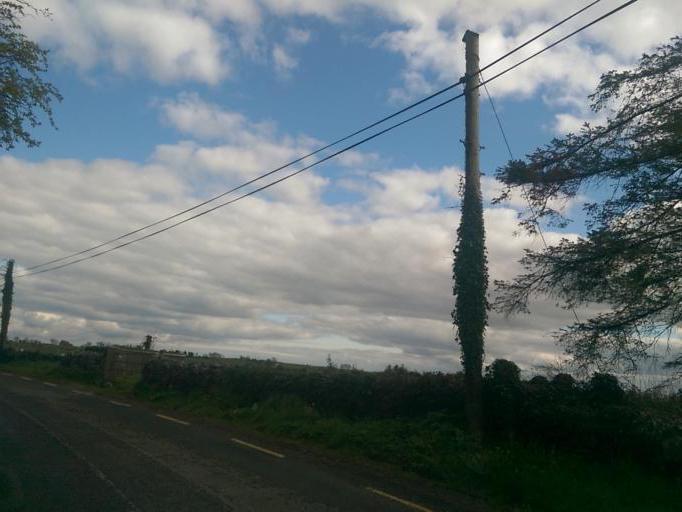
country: IE
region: Connaught
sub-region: County Galway
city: Loughrea
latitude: 53.4193
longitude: -8.5231
